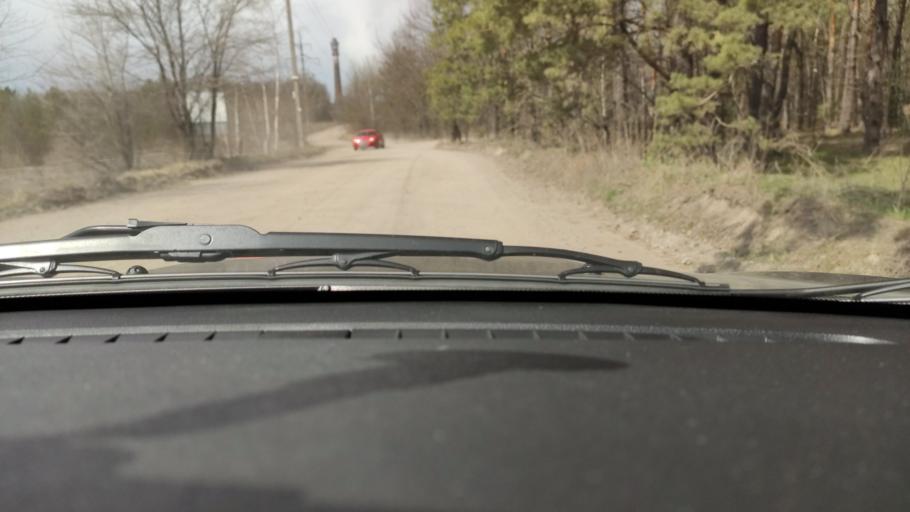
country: RU
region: Voronezj
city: Shilovo
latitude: 51.5555
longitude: 39.1170
